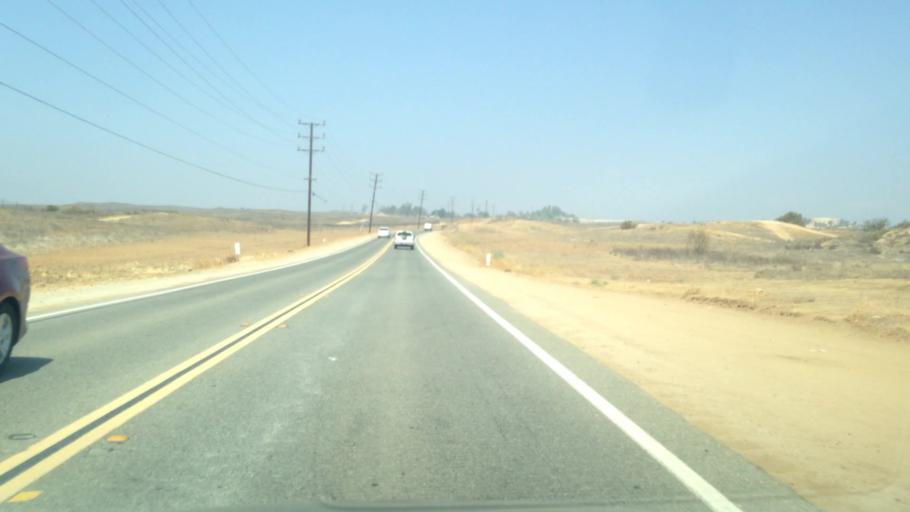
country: US
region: California
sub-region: Riverside County
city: Woodcrest
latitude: 33.8479
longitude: -117.3829
